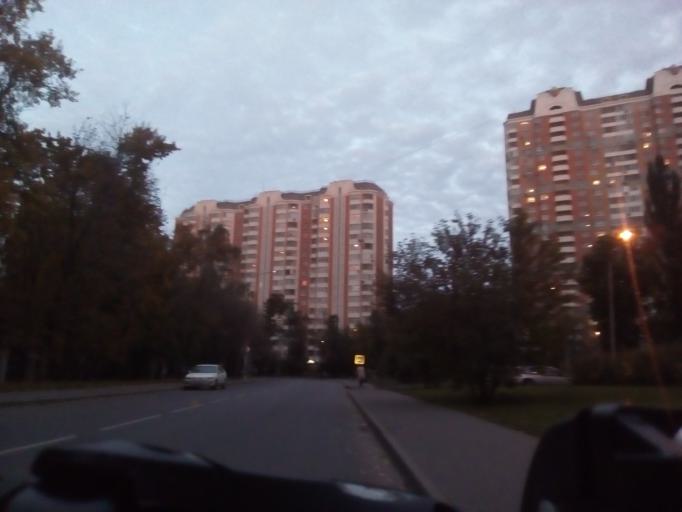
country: RU
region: Moscow
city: Leonovo
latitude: 55.8556
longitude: 37.6469
